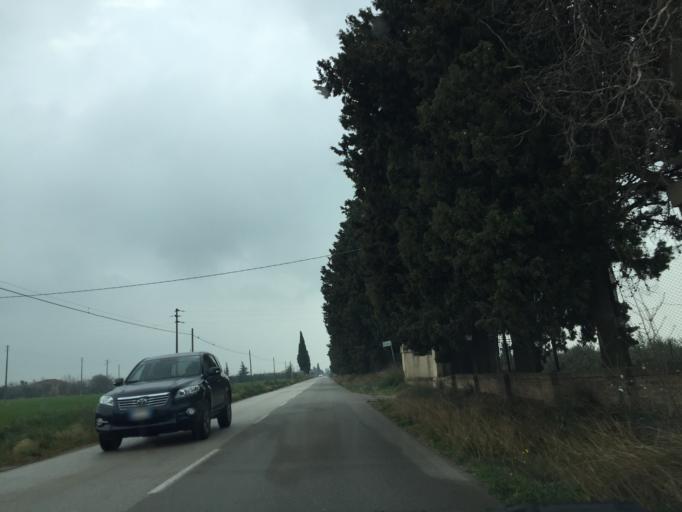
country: IT
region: Apulia
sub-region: Provincia di Foggia
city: Foggia
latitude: 41.4190
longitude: 15.4608
